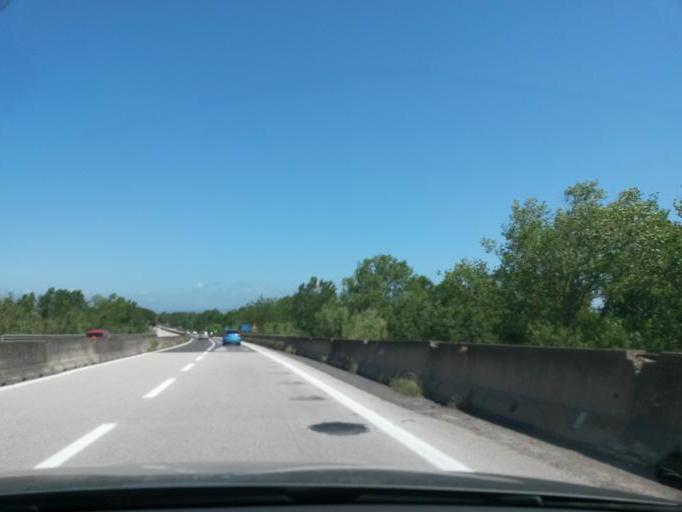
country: IT
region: Tuscany
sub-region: Provincia di Livorno
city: Donoratico
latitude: 43.1841
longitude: 10.5659
